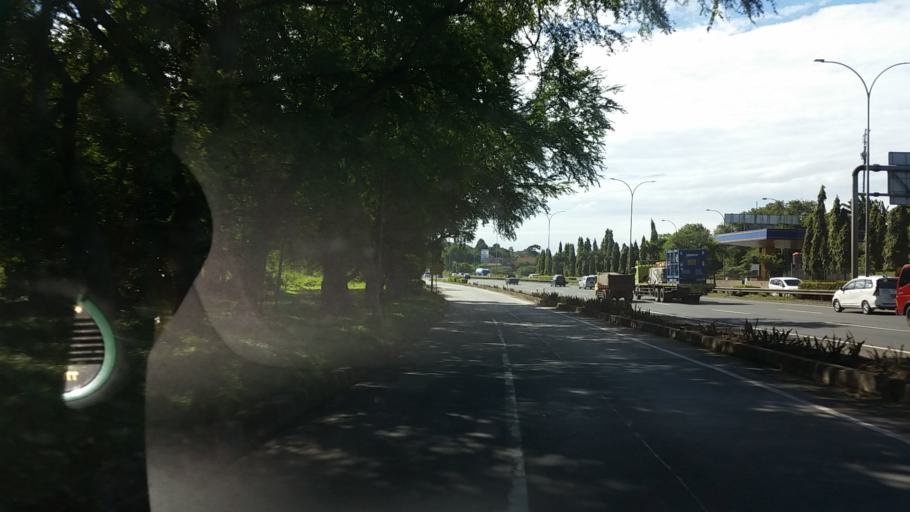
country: ID
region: Banten
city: South Tangerang
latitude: -6.2758
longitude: 106.7682
